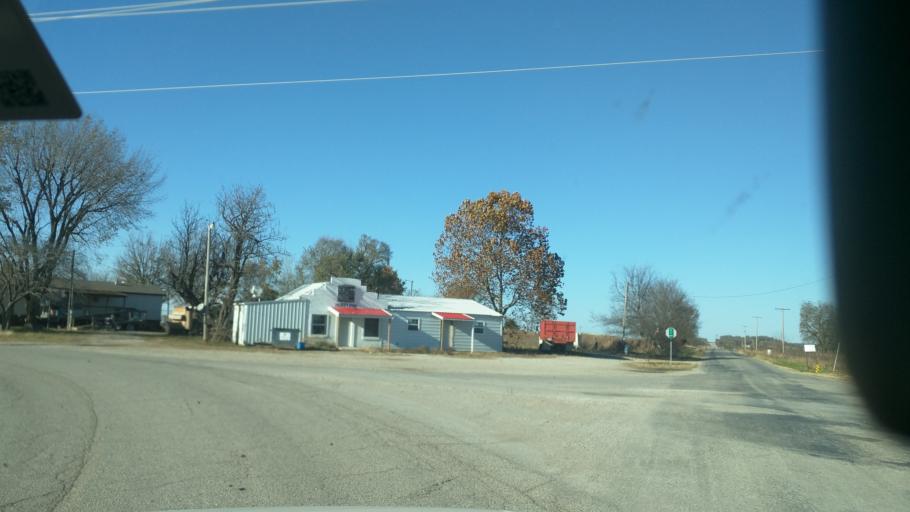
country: US
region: Oklahoma
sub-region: Nowata County
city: Nowata
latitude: 36.7714
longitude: -95.5396
